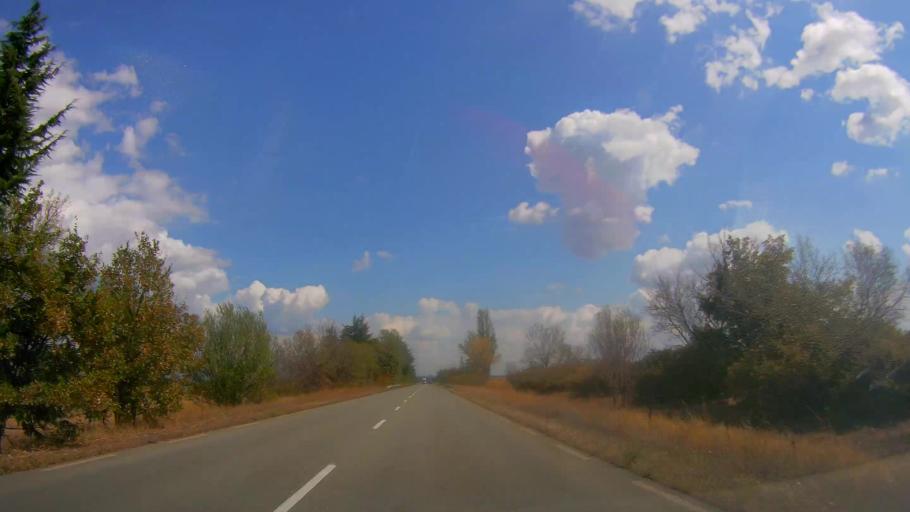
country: BG
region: Sliven
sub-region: Obshtina Tvurditsa
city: Tvurditsa
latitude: 42.6555
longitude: 25.9359
